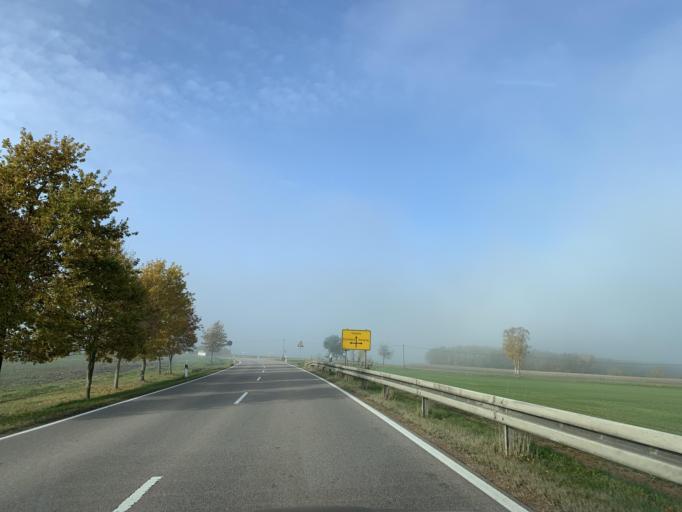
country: DE
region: Bavaria
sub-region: Upper Palatinate
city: Brunn
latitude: 49.2415
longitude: 12.2132
